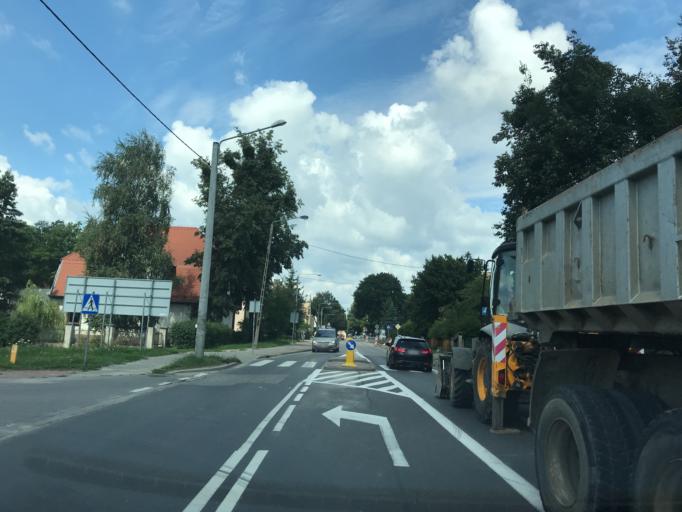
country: PL
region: Warmian-Masurian Voivodeship
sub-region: Powiat ostrodzki
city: Ostroda
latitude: 53.6943
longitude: 19.9750
